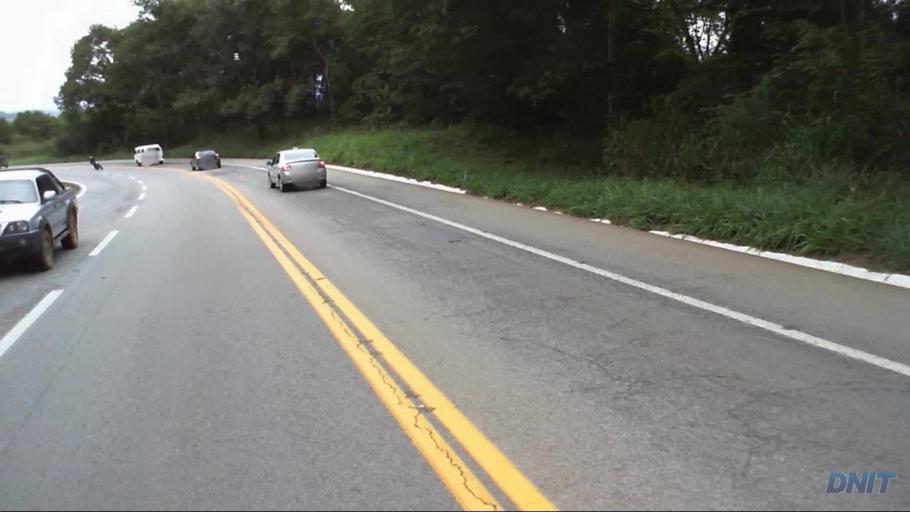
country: BR
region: Minas Gerais
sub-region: Caete
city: Caete
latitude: -19.7423
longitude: -43.5199
